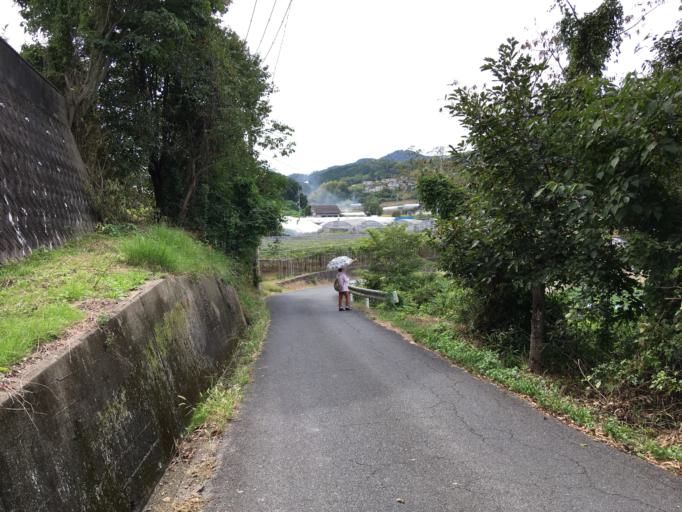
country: JP
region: Nara
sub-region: Ikoma-shi
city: Ikoma
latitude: 34.6184
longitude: 135.7001
